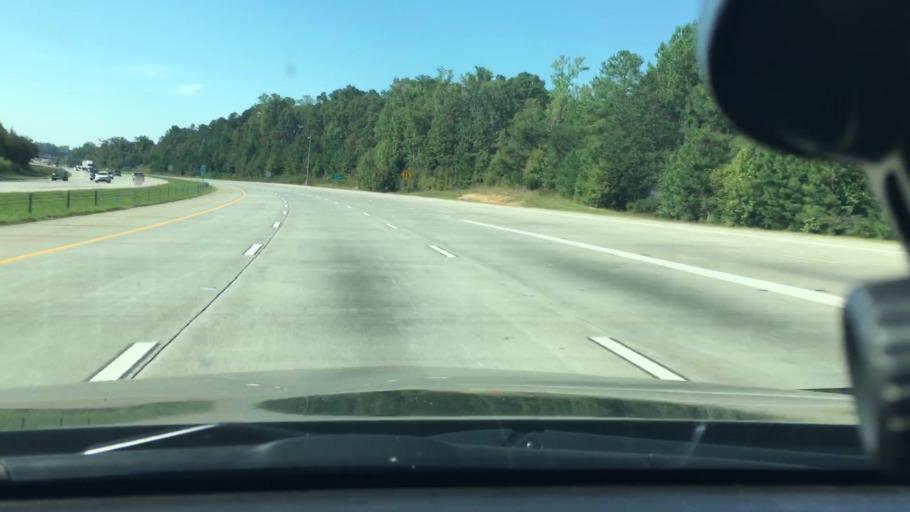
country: US
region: North Carolina
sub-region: Mecklenburg County
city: Huntersville
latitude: 35.3612
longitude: -80.8528
